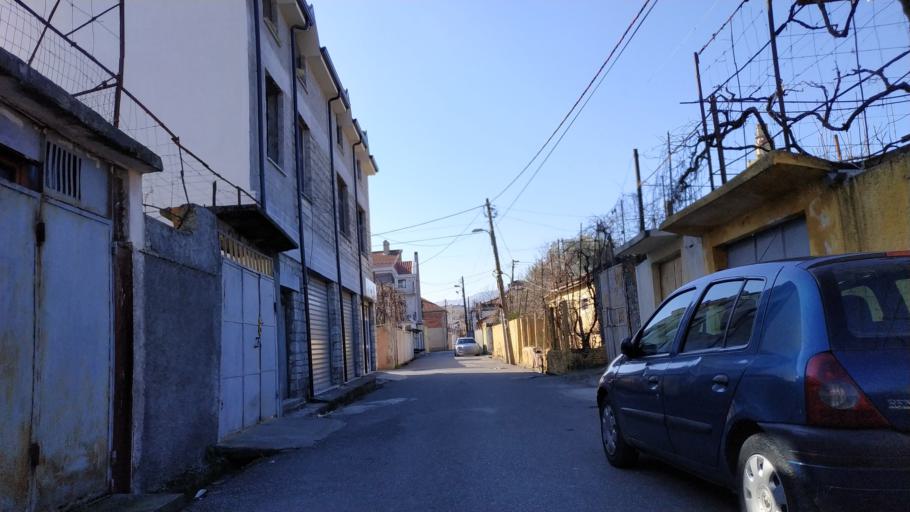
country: AL
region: Shkoder
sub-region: Rrethi i Shkodres
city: Shkoder
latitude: 42.0651
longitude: 19.5220
